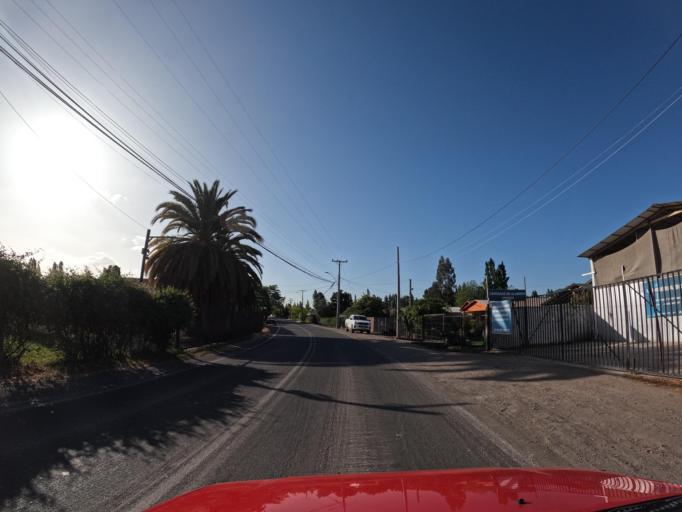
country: CL
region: O'Higgins
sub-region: Provincia de Colchagua
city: Santa Cruz
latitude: -34.6546
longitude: -71.3423
